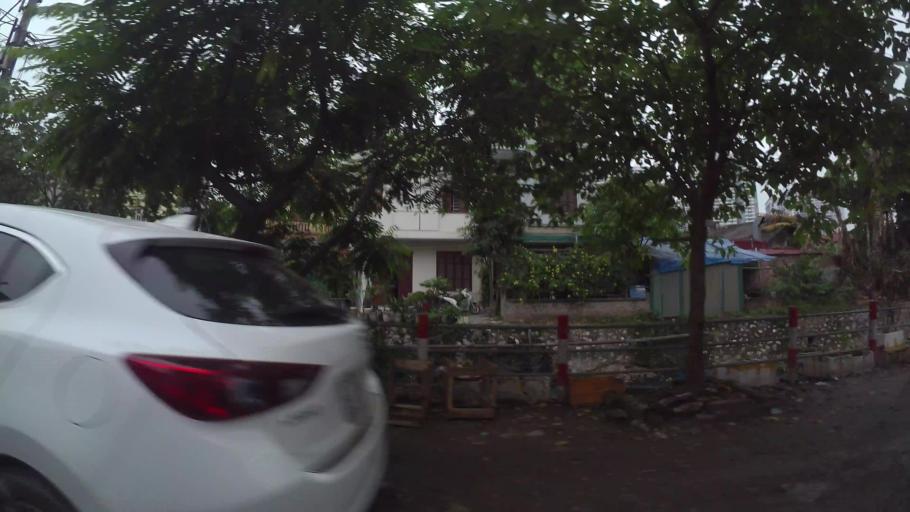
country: VN
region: Ha Noi
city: Hai BaTrung
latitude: 20.9868
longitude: 105.8694
